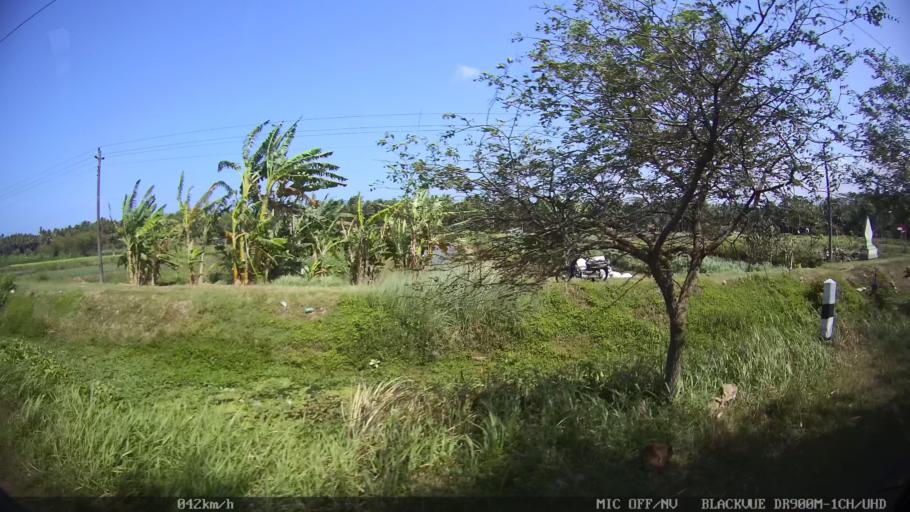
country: ID
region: Daerah Istimewa Yogyakarta
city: Srandakan
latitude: -7.9284
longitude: 110.1560
